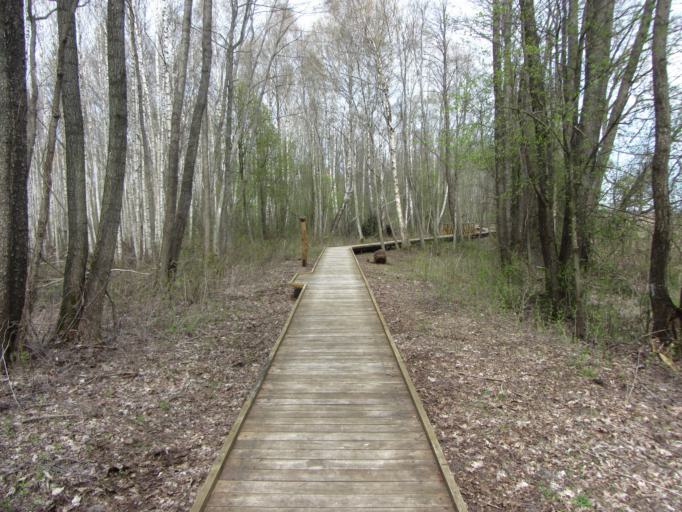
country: LT
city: Zarasai
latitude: 55.5793
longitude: 26.1525
